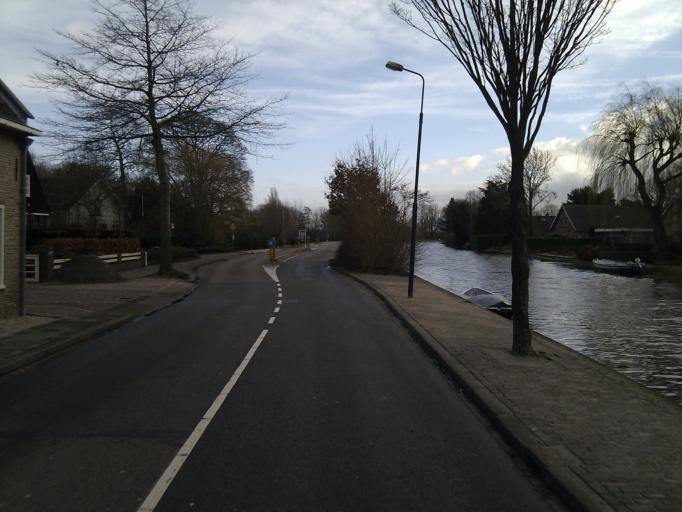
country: NL
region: North Holland
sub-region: Gemeente Amsterdam
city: Amsterdam-Zuidoost
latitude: 52.2694
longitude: 4.9769
